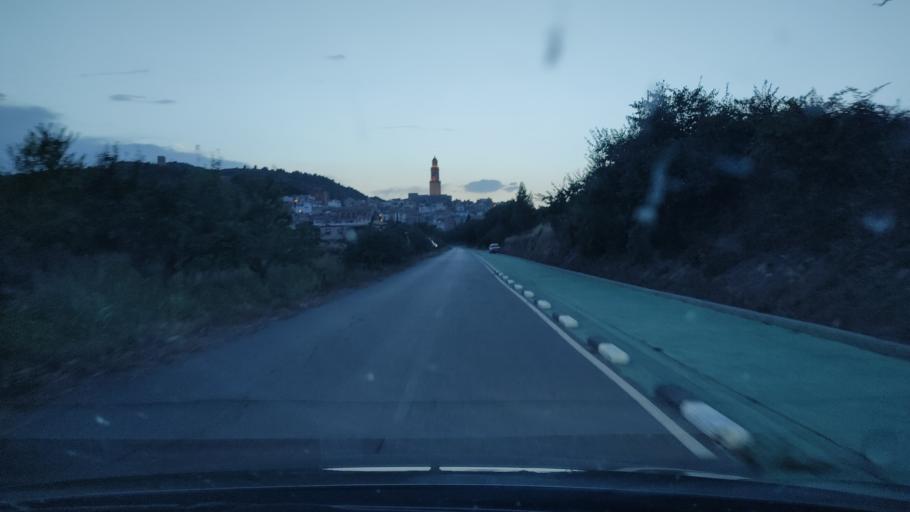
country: ES
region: Valencia
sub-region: Provincia de Castello
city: Jerica
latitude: 39.9091
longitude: -0.5633
